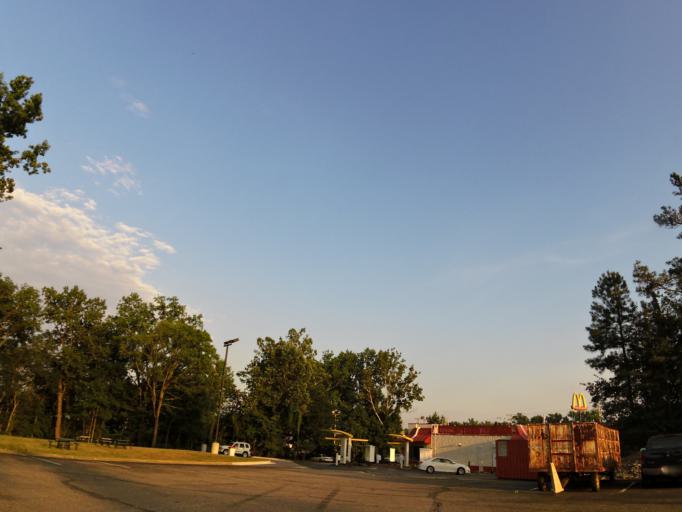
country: US
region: Tennessee
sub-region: Henry County
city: Paris
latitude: 36.2906
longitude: -88.3137
